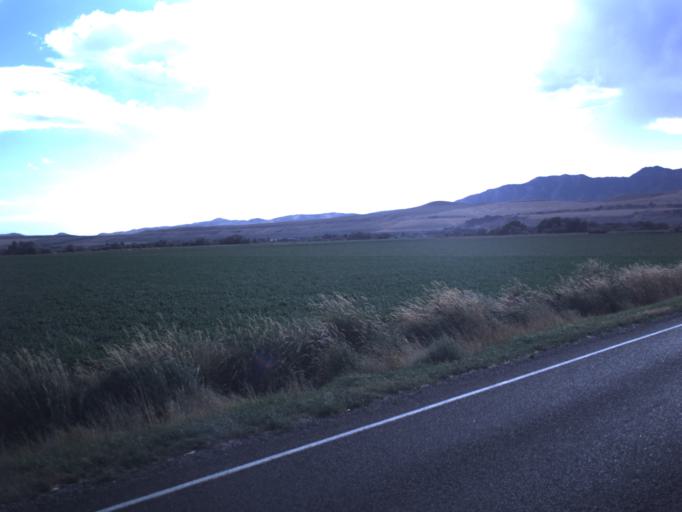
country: US
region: Utah
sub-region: Cache County
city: Lewiston
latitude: 41.9755
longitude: -111.9188
